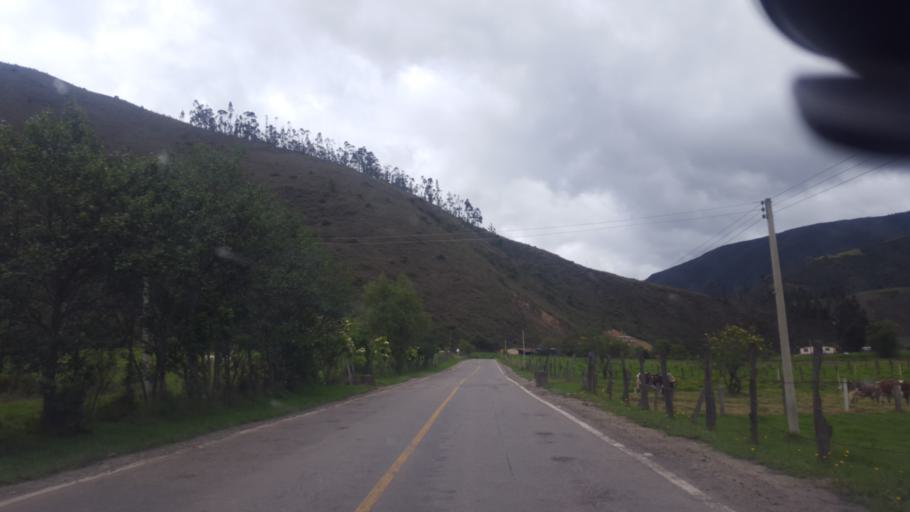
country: CO
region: Boyaca
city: Belen
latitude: 6.0116
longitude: -72.8300
